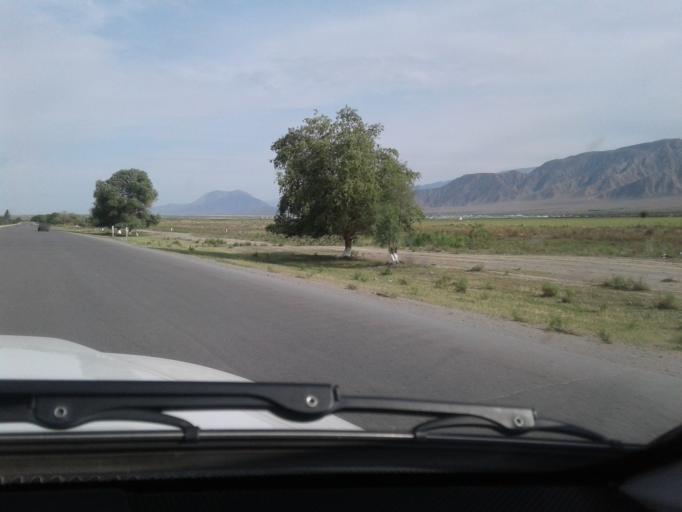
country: TM
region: Ahal
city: Arcabil
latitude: 38.1865
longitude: 57.8524
